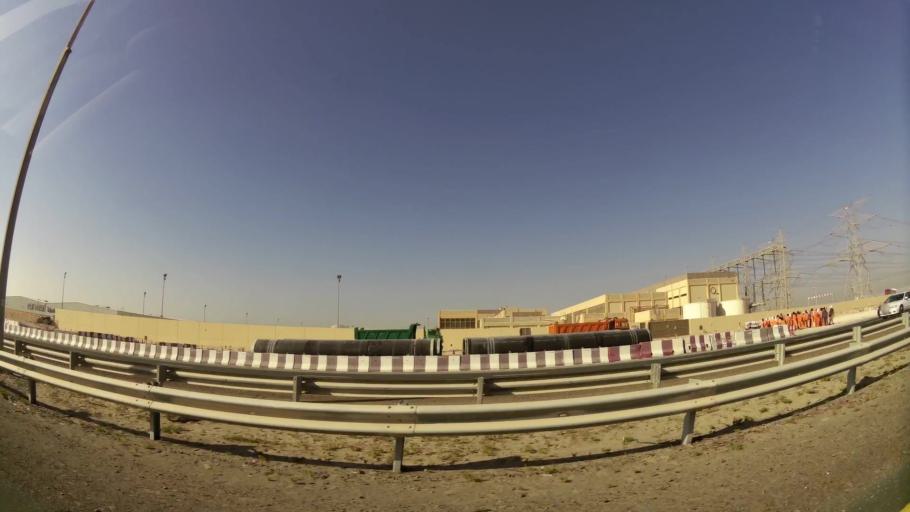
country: AE
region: Dubai
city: Dubai
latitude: 24.9399
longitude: 55.0712
